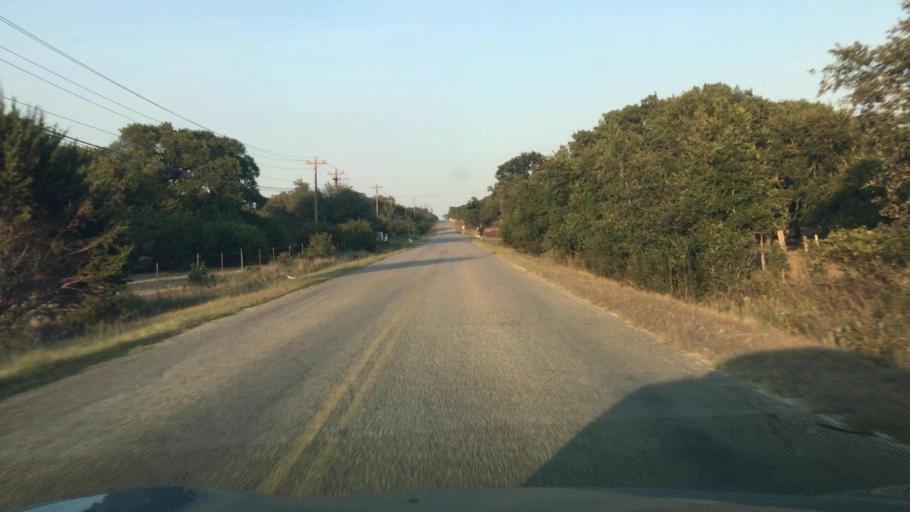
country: US
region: Texas
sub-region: Hays County
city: Dripping Springs
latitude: 30.1532
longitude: -98.0204
